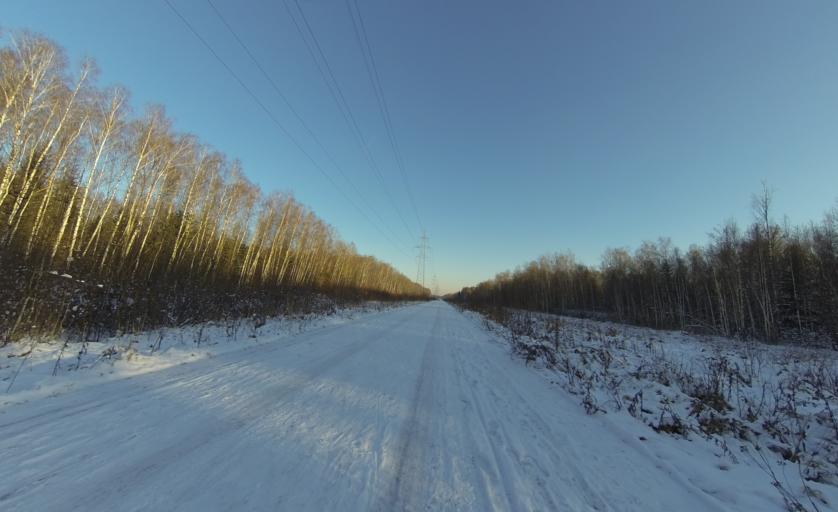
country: RU
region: Moscow
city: Babushkin
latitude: 55.8425
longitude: 37.7298
